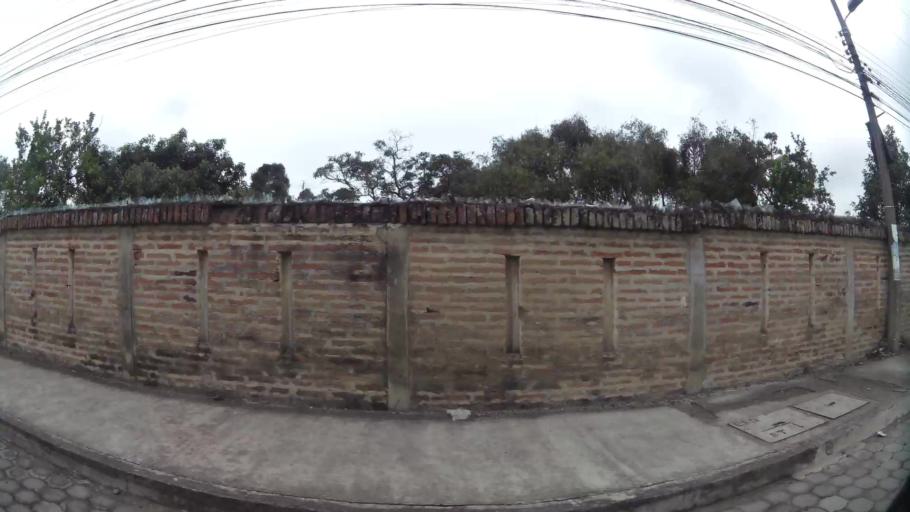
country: EC
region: Pichincha
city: Sangolqui
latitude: -0.2799
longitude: -78.4681
